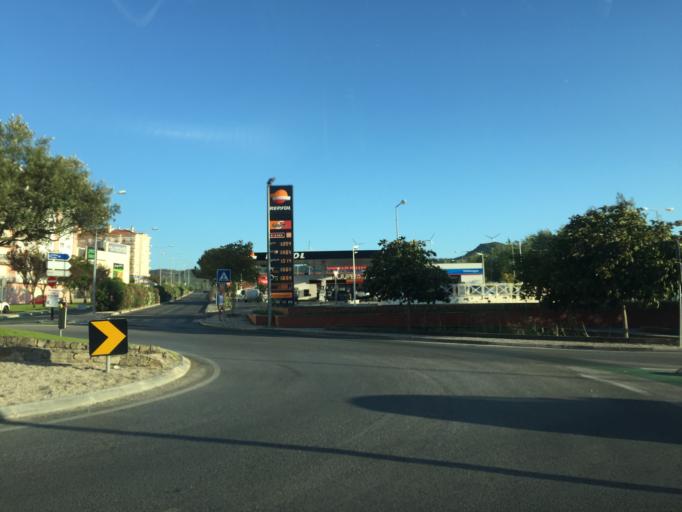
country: PT
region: Lisbon
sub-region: Torres Vedras
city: Torres Vedras
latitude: 39.0827
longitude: -9.2606
